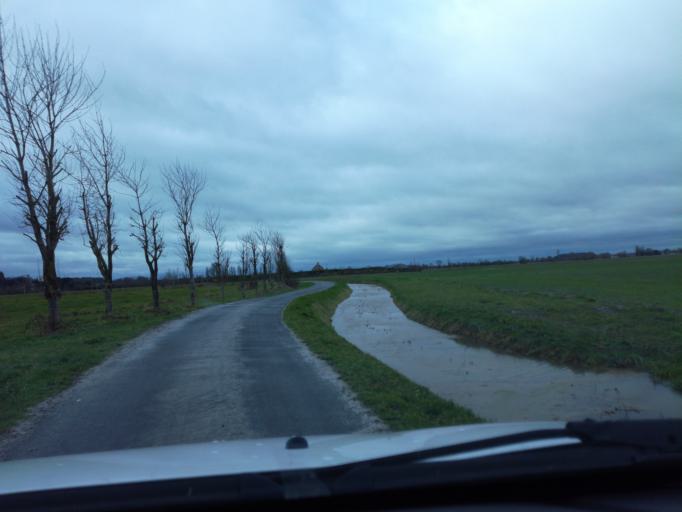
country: FR
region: Brittany
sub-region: Departement d'Ille-et-Vilaine
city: Cherrueix
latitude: 48.5815
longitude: -1.6916
